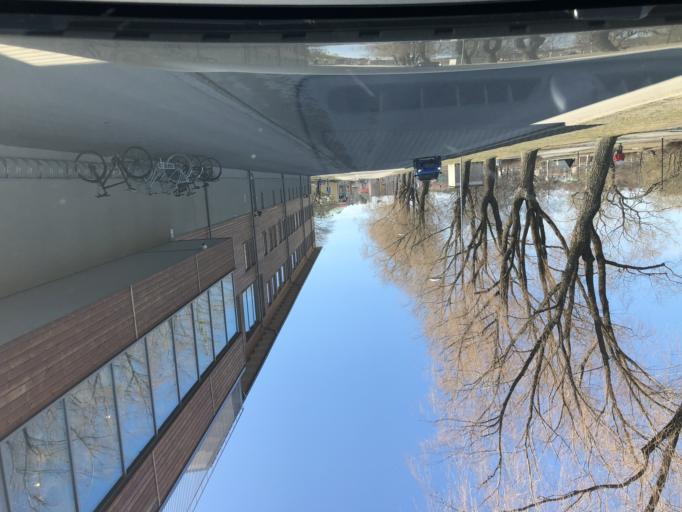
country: SE
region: Gaevleborg
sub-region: Hudiksvalls Kommun
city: Hudiksvall
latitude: 61.7293
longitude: 17.1083
